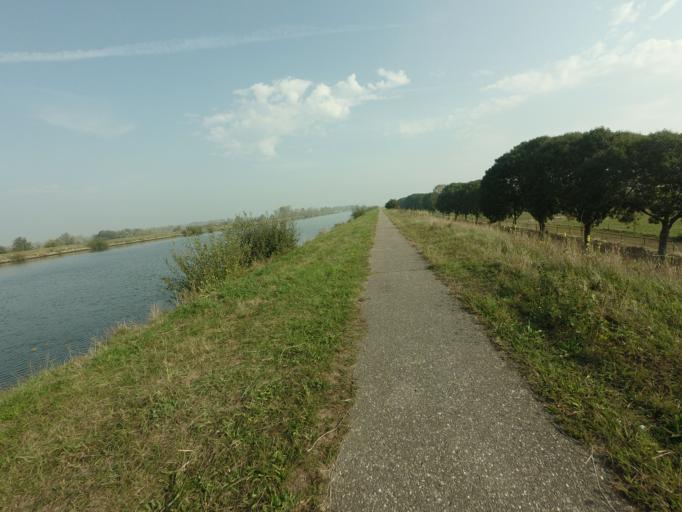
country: NL
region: Limburg
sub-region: Gemeente Maasgouw
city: Maasbracht
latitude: 51.1315
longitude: 5.8702
